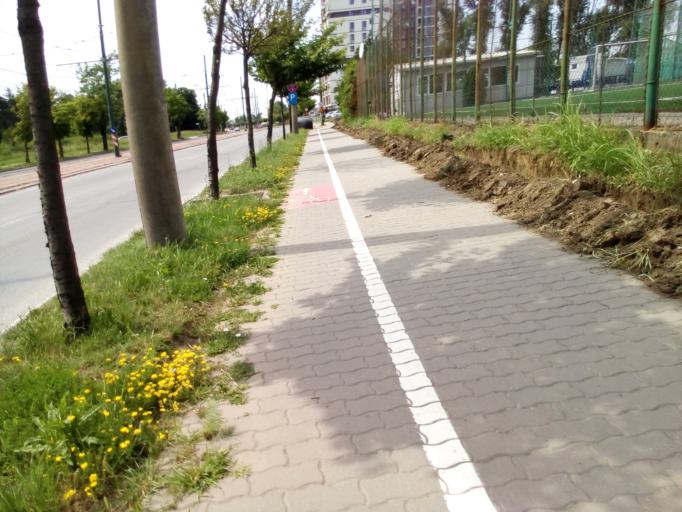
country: RO
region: Timis
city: Timisoara
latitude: 45.7353
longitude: 21.2552
